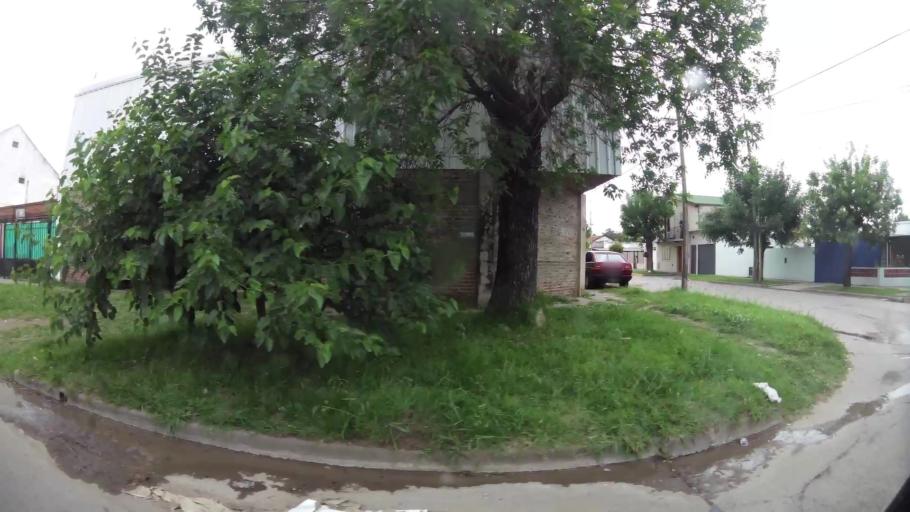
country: AR
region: Buenos Aires
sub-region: Partido de Zarate
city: Zarate
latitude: -34.1188
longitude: -59.0225
